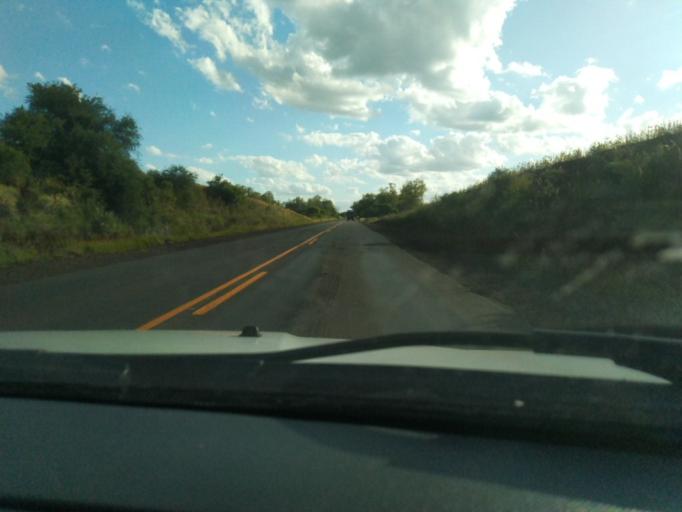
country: AR
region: Corrientes
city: Garruchos
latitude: -28.5467
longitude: -55.5591
